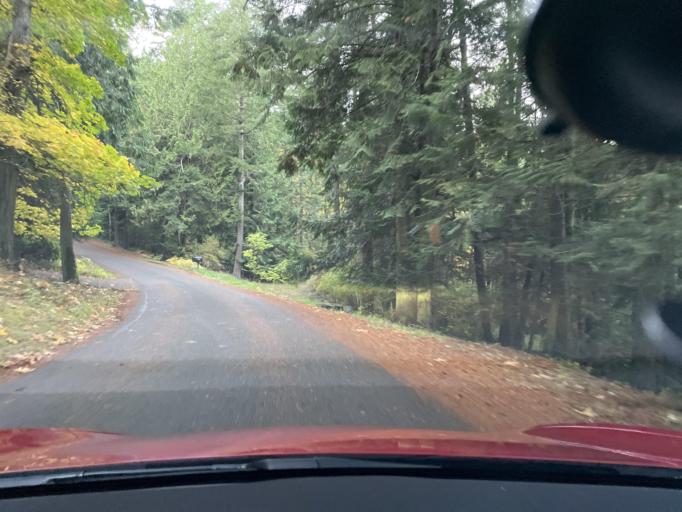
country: US
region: Washington
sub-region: San Juan County
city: Friday Harbor
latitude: 48.6009
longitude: -123.1511
